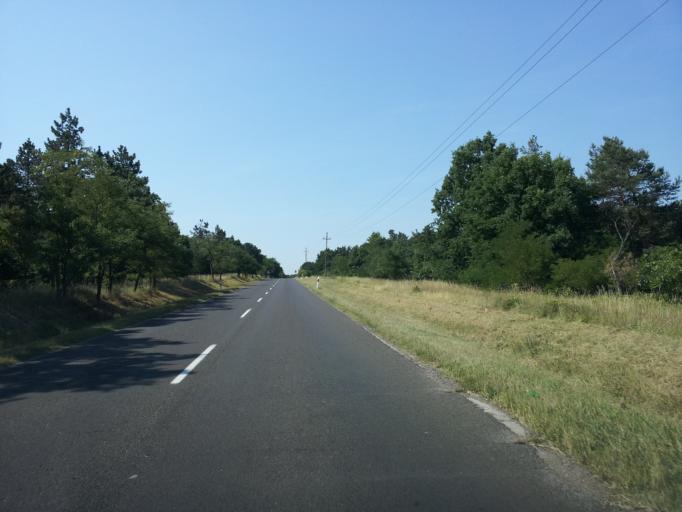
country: HU
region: Fejer
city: Pakozd
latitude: 47.2488
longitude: 18.5120
